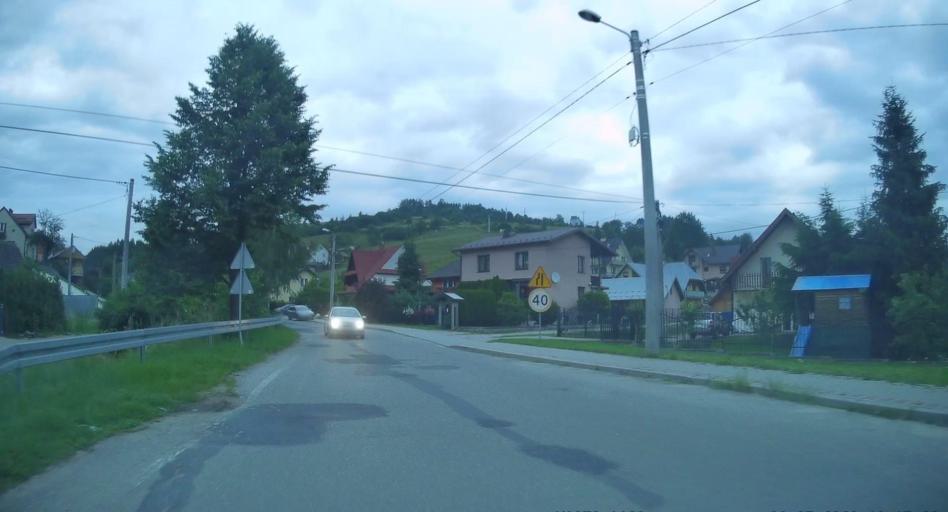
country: PL
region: Lesser Poland Voivodeship
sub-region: Powiat nowosadecki
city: Muszyna
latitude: 49.3650
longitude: 20.9263
